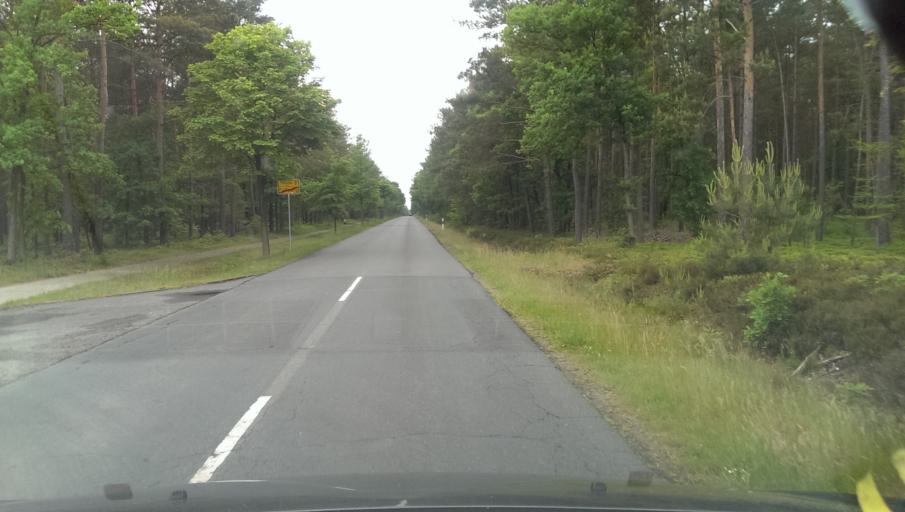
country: DE
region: Lower Saxony
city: Fassberg
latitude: 52.8950
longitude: 10.1544
